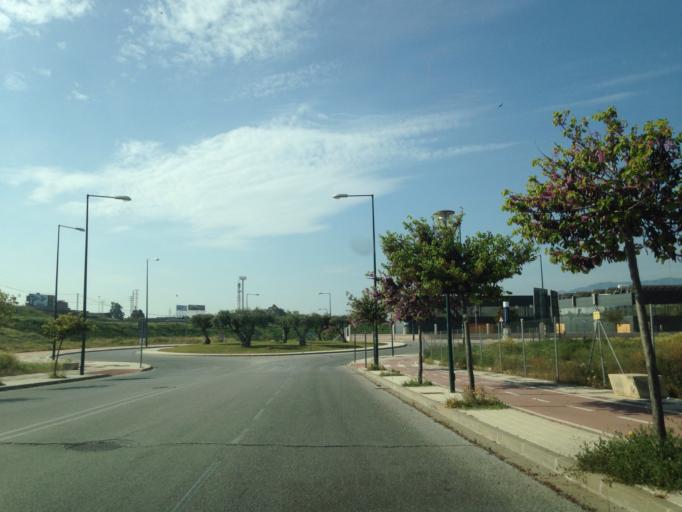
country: ES
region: Andalusia
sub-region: Provincia de Malaga
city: Malaga
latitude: 36.7168
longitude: -4.4899
